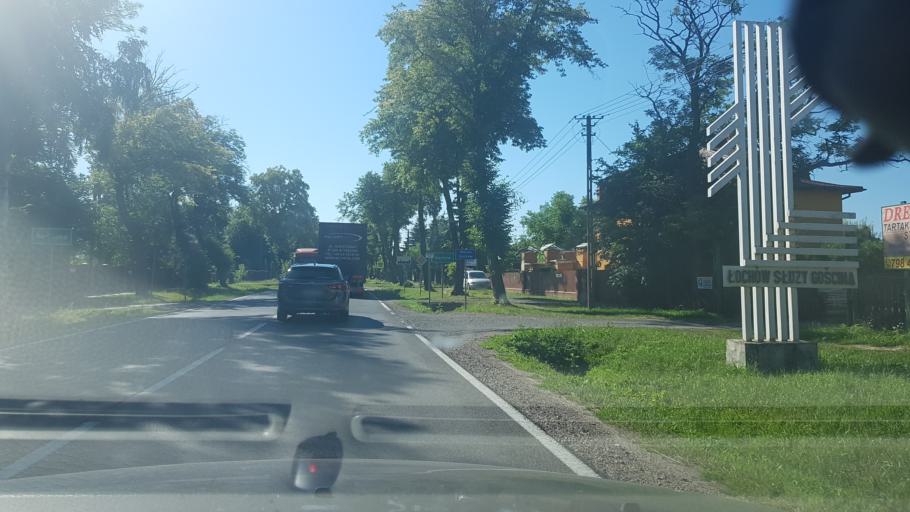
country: PL
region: Masovian Voivodeship
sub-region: Powiat wegrowski
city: Lochow
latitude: 52.5360
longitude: 21.6726
